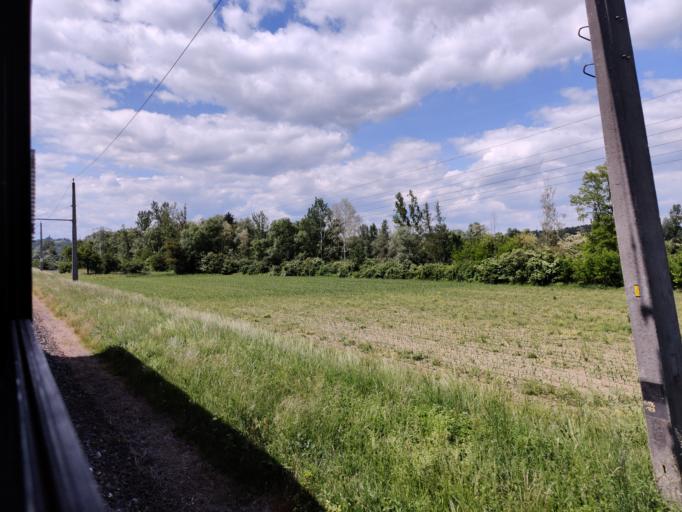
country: AT
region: Styria
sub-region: Politischer Bezirk Leibnitz
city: Wildon
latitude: 46.8813
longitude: 15.5246
